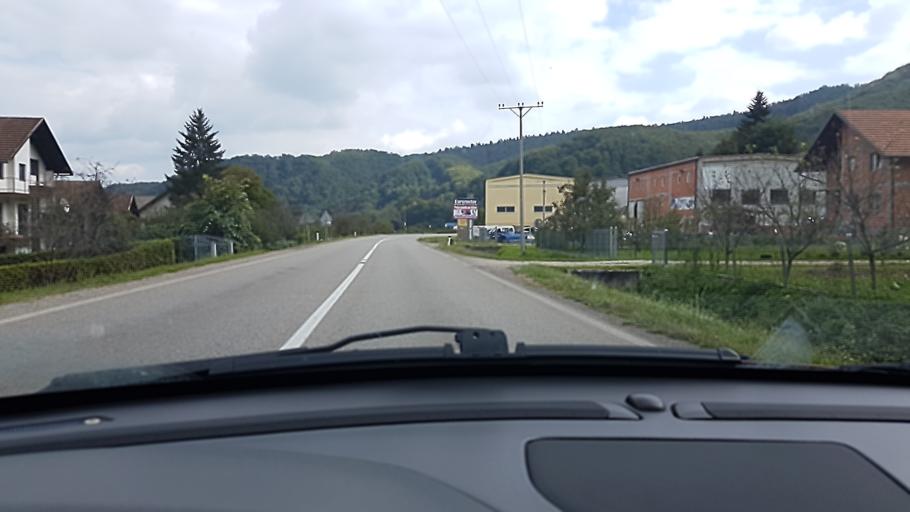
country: BA
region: Republika Srpska
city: Teslic
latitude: 44.6354
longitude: 17.8660
